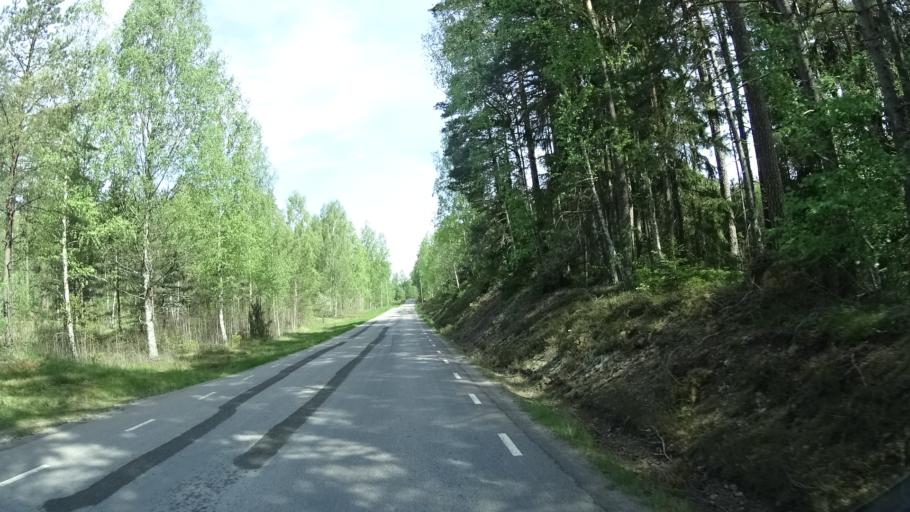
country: SE
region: OEstergoetland
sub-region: Finspangs Kommun
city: Finspang
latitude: 58.7458
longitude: 15.8283
